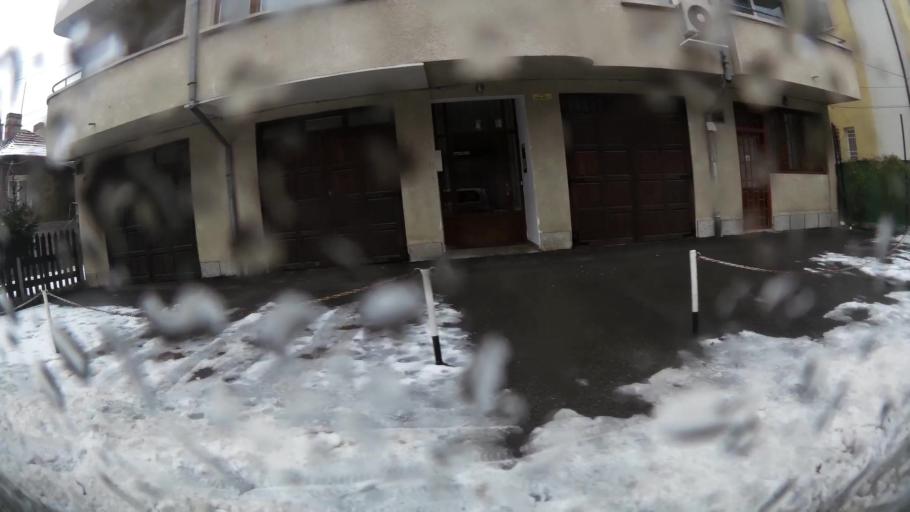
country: BG
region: Sofia-Capital
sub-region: Stolichna Obshtina
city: Sofia
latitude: 42.6744
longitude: 23.2661
